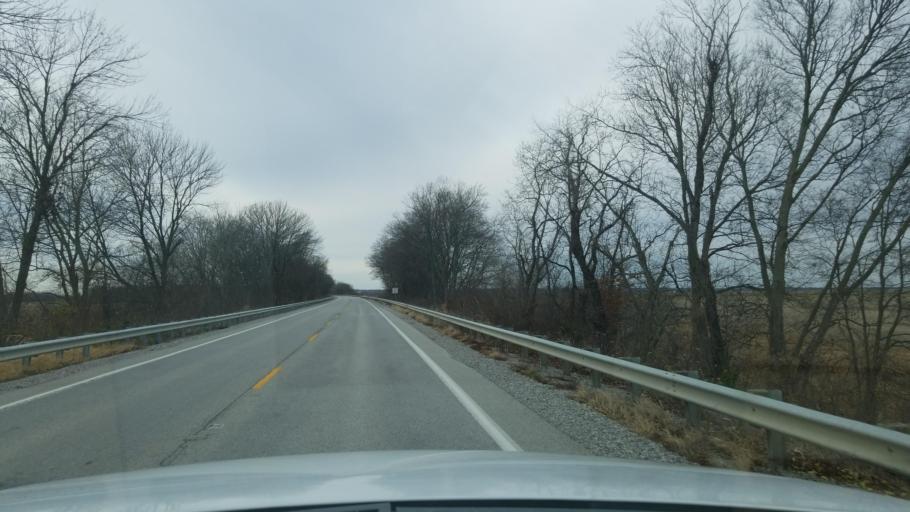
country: US
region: Indiana
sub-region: Posey County
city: Mount Vernon
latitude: 37.9434
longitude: -88.0490
